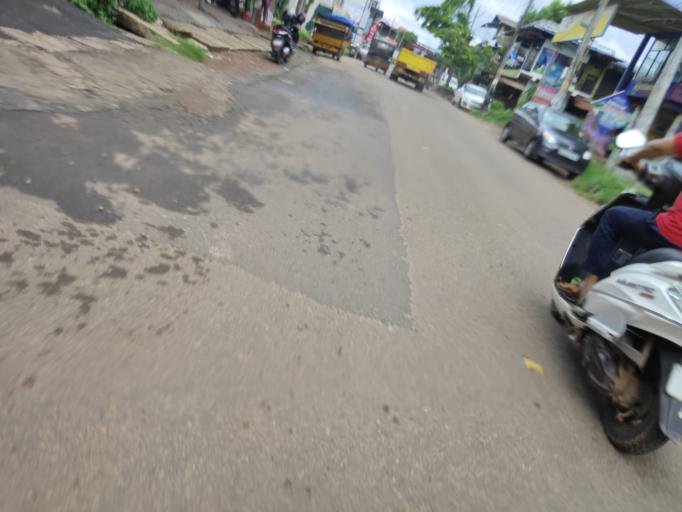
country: IN
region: Kerala
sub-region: Malappuram
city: Manjeri
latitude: 11.1951
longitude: 76.2380
